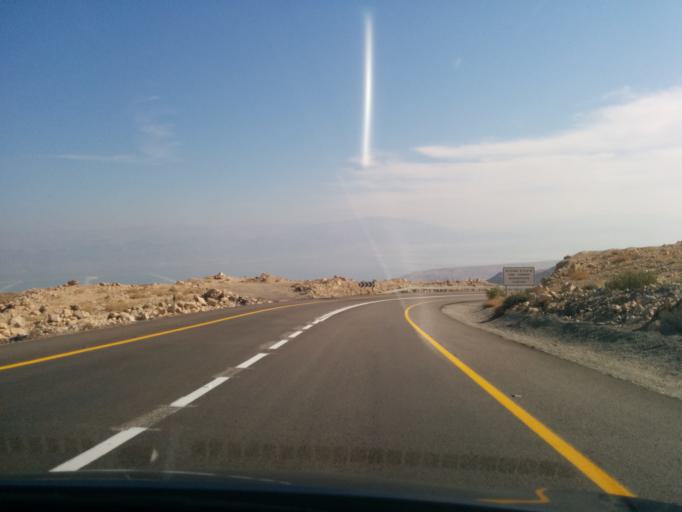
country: IL
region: Southern District
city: `En Boqeq
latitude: 31.1584
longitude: 35.3331
